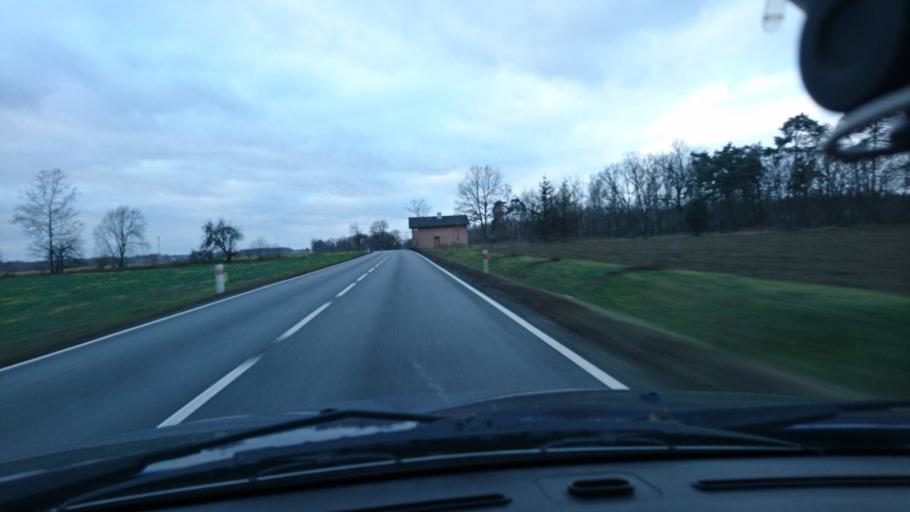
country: PL
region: Lodz Voivodeship
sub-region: Powiat wieruszowski
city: Boleslawiec
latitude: 51.1525
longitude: 18.1808
